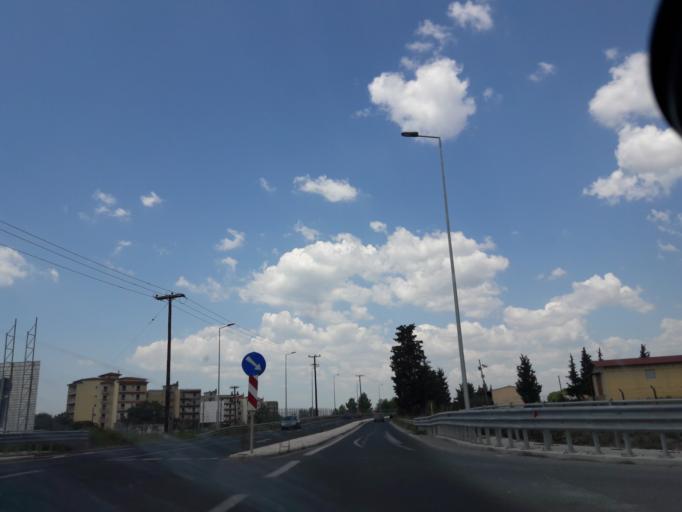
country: GR
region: Central Macedonia
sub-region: Nomos Thessalonikis
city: Thermi
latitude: 40.5331
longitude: 23.0392
